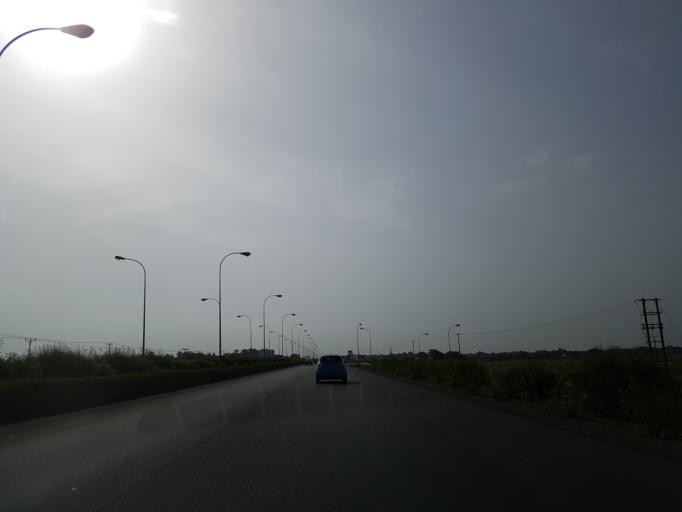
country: OM
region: Al Batinah
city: Al Sohar
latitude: 24.4089
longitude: 56.6473
